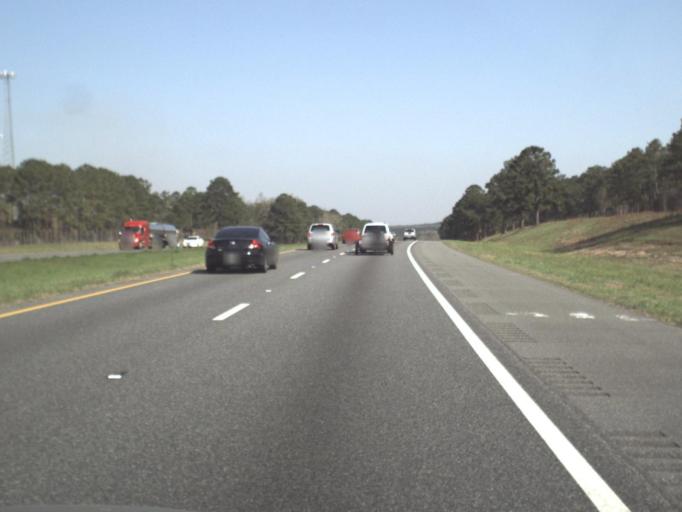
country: US
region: Florida
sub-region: Gadsden County
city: Quincy
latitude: 30.5305
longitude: -84.5358
